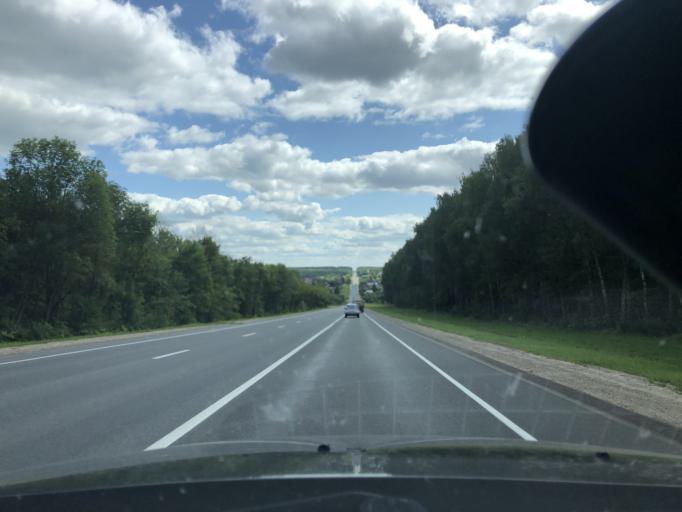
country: RU
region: Tula
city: Gorelki
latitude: 54.3113
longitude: 37.5668
